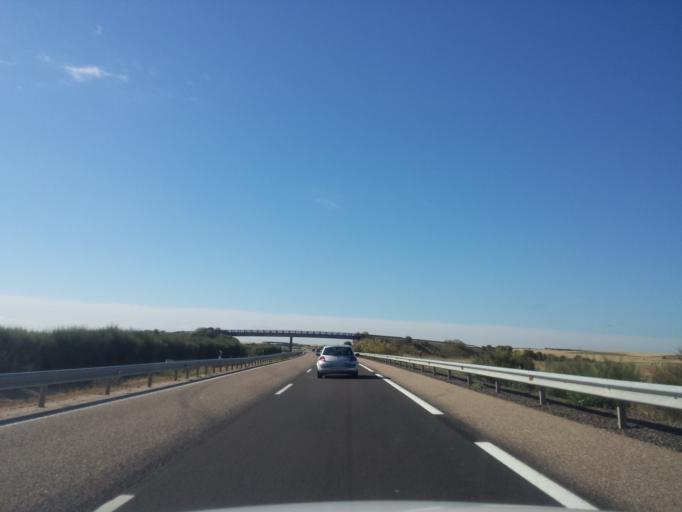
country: ES
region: Castille and Leon
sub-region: Provincia de Zamora
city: Matilla de Arzon
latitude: 42.1038
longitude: -5.6602
